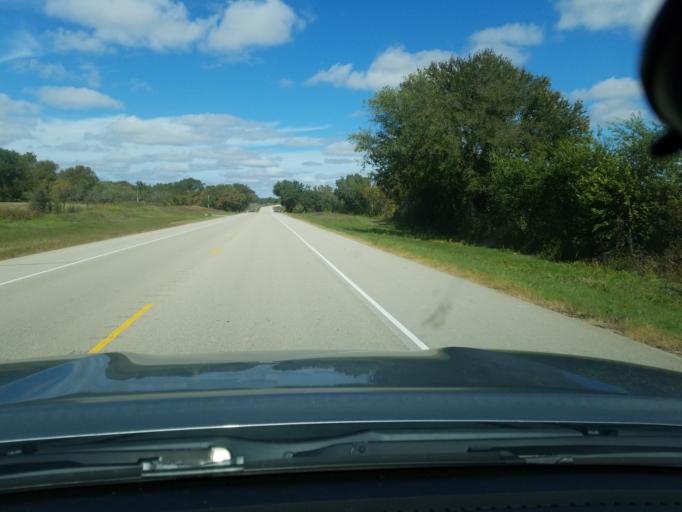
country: US
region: Texas
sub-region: Hamilton County
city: Hamilton
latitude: 31.6062
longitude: -98.1583
